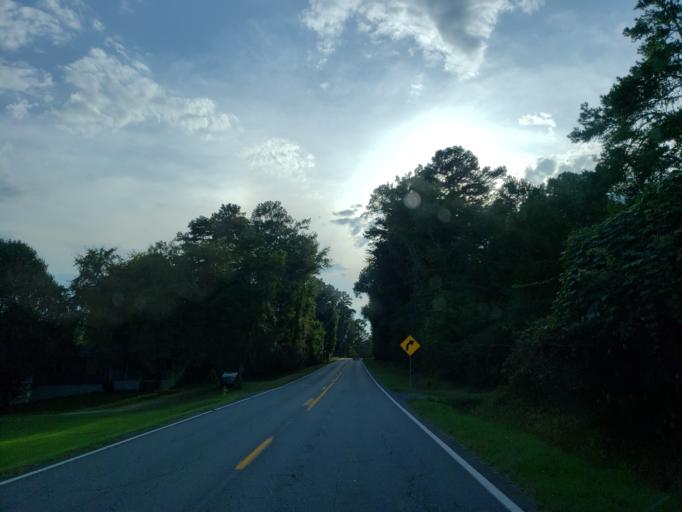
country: US
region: Georgia
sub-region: Bartow County
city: Euharlee
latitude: 34.2379
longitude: -84.9345
